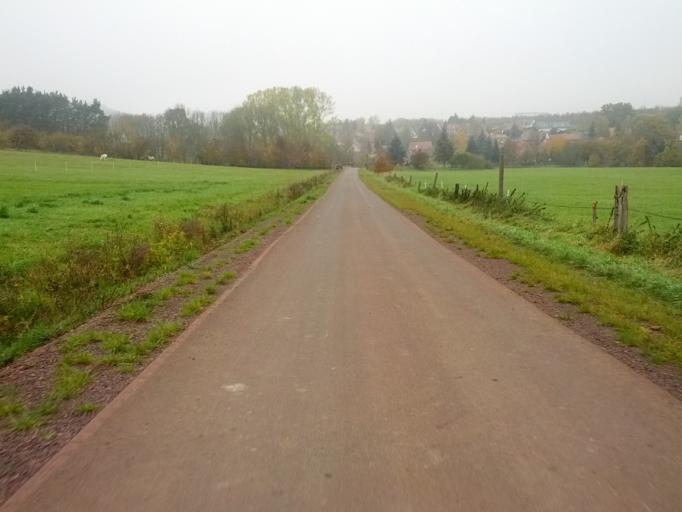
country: DE
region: Thuringia
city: Bischofroda
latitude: 50.9878
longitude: 10.3824
